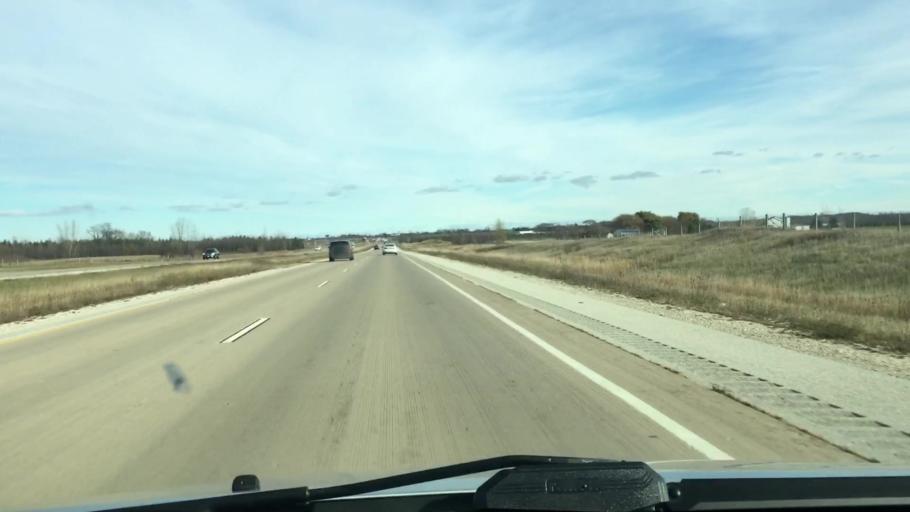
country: US
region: Wisconsin
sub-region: Kewaunee County
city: Luxemburg
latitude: 44.7161
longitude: -87.6485
